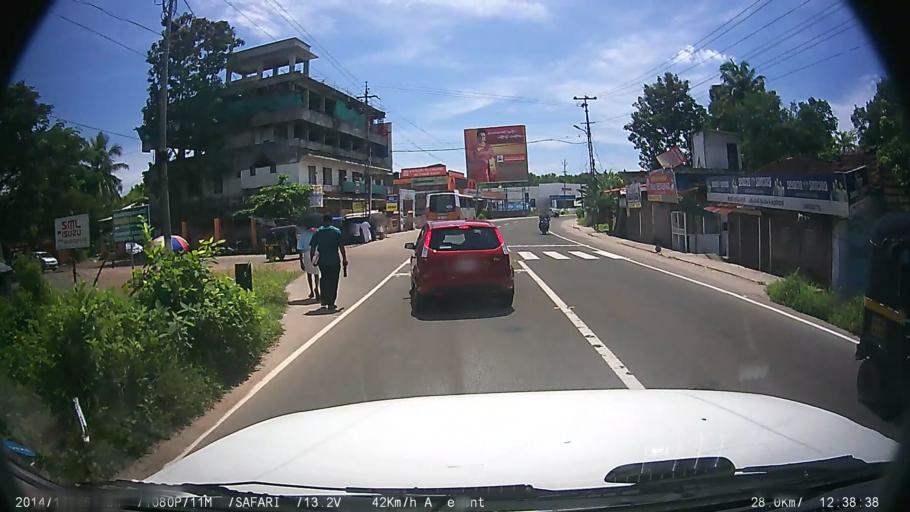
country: IN
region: Kerala
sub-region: Kottayam
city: Kottayam
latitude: 9.5671
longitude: 76.5195
